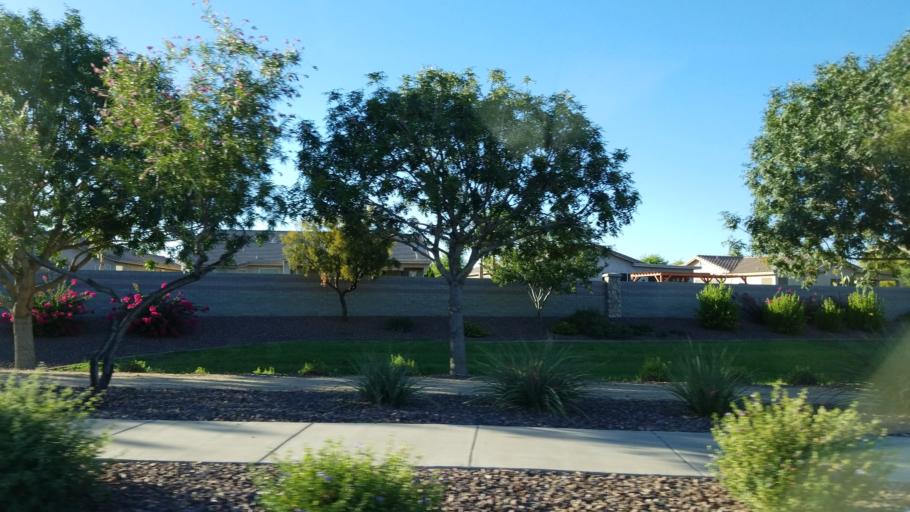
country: US
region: Arizona
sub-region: Maricopa County
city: Laveen
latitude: 33.3775
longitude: -112.2179
